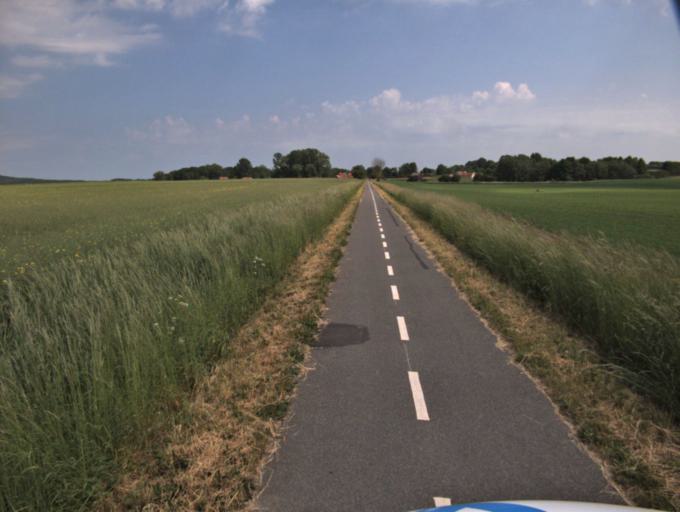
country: SE
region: Skane
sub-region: Kristianstads Kommun
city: Kristianstad
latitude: 56.0701
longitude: 14.1975
